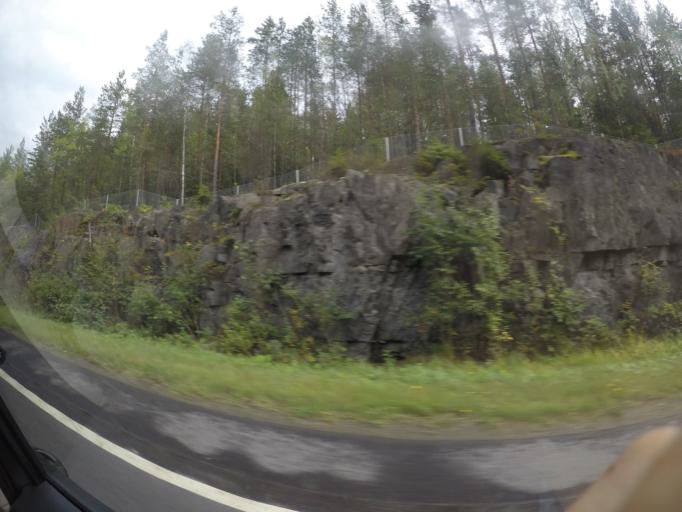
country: FI
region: Haeme
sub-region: Haemeenlinna
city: Parola
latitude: 61.0877
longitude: 24.4000
